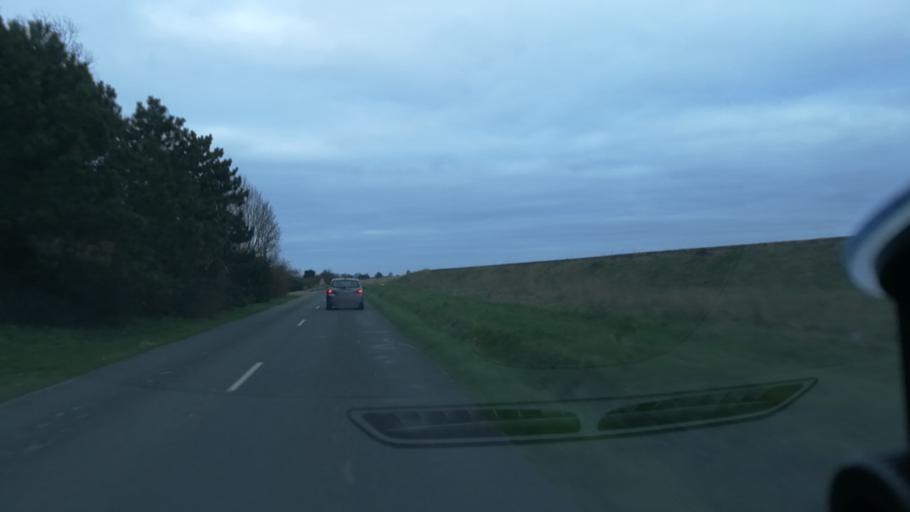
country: FR
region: Lower Normandy
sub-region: Departement de la Manche
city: Saint-Vaast-la-Hougue
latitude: 49.6016
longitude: -1.2610
